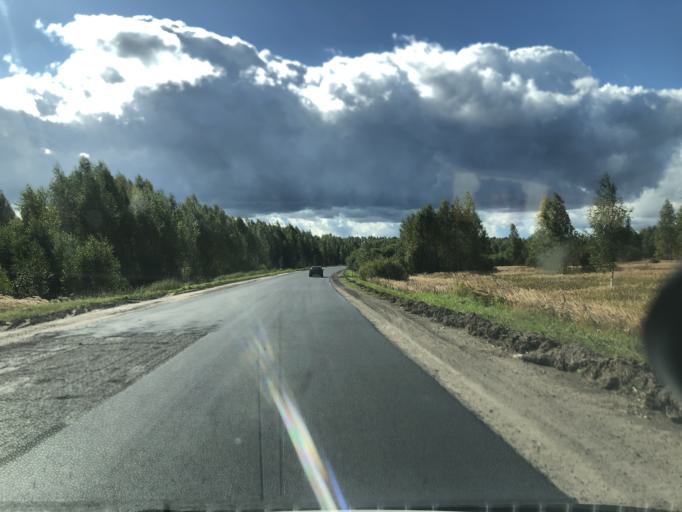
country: RU
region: Jaroslavl
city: Petrovsk
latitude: 56.9671
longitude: 39.3859
